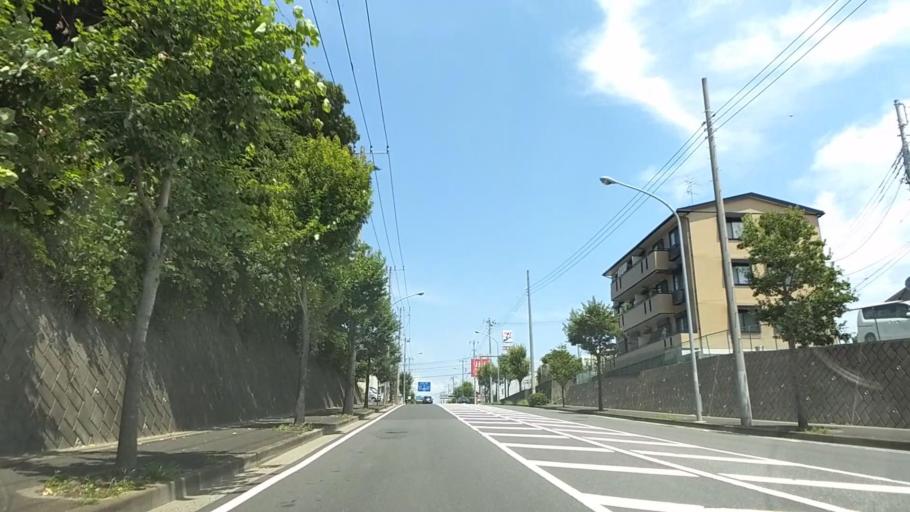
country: JP
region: Kanagawa
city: Minami-rinkan
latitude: 35.4546
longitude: 139.4821
